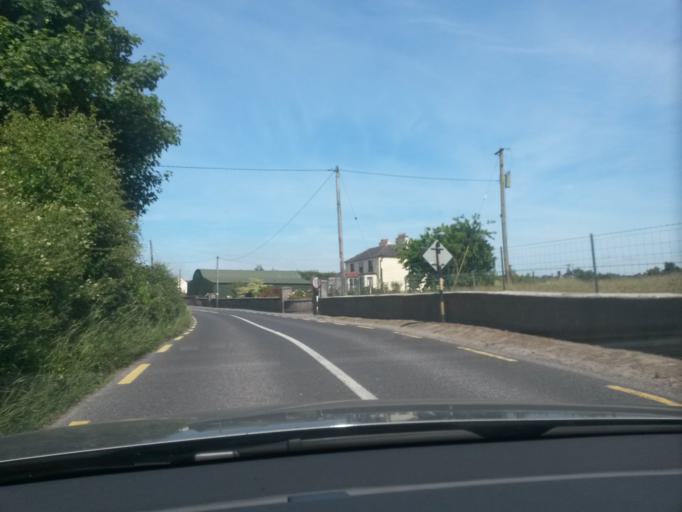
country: IE
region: Leinster
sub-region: Kildare
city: Eadestown
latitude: 53.2019
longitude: -6.5799
